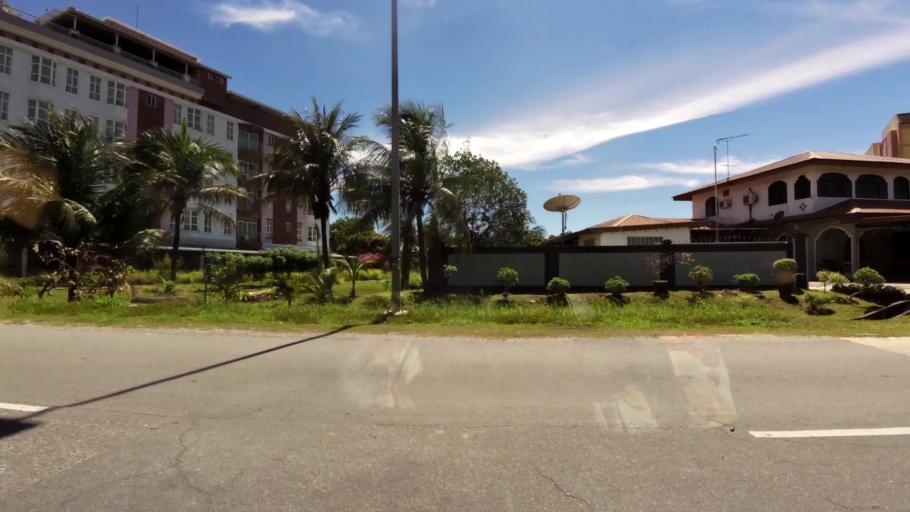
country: BN
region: Brunei and Muara
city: Bandar Seri Begawan
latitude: 5.0260
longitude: 115.0619
